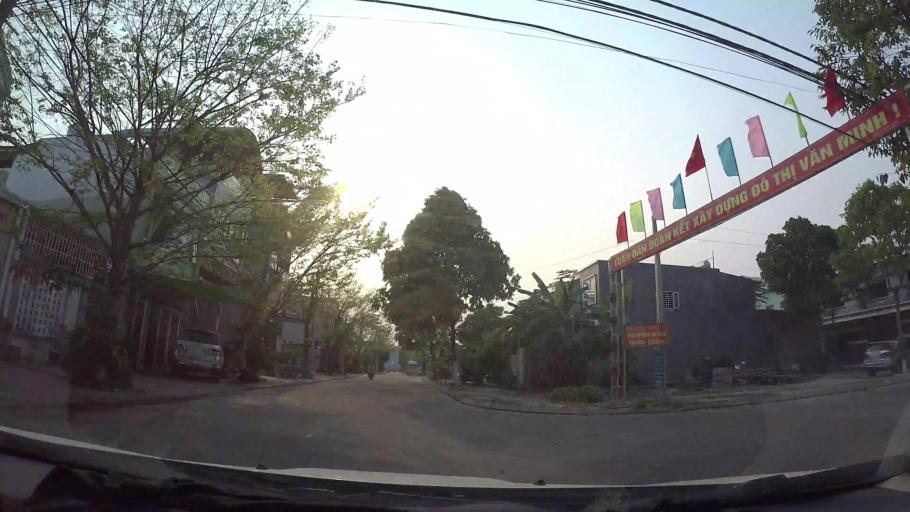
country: VN
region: Da Nang
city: Cam Le
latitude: 16.0173
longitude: 108.1955
